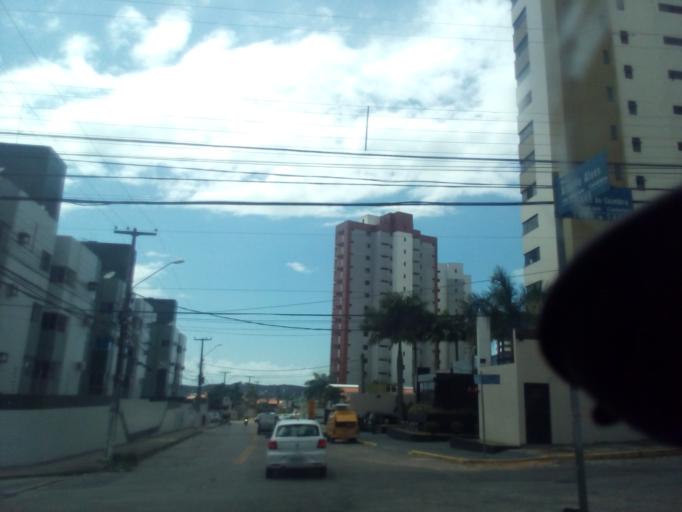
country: BR
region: Rio Grande do Norte
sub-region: Natal
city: Natal
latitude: -5.8390
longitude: -35.2153
